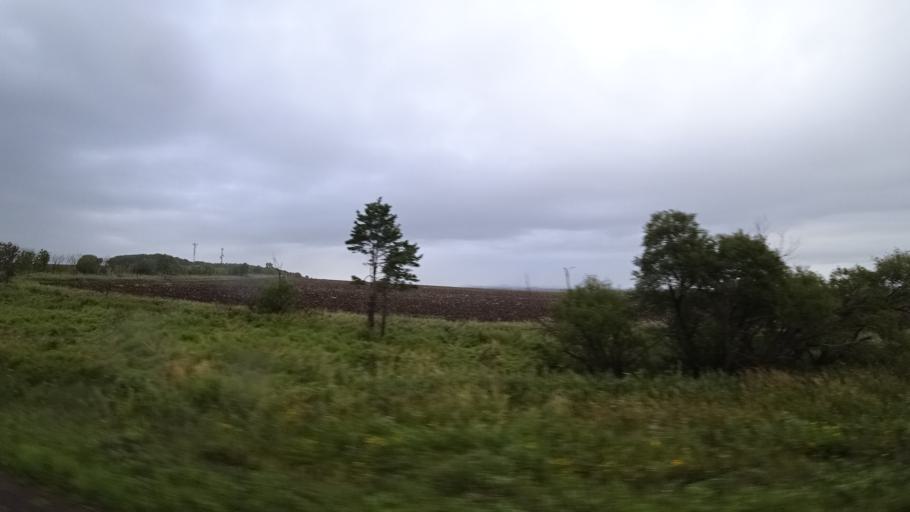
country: RU
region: Primorskiy
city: Chernigovka
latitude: 44.3654
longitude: 132.5388
